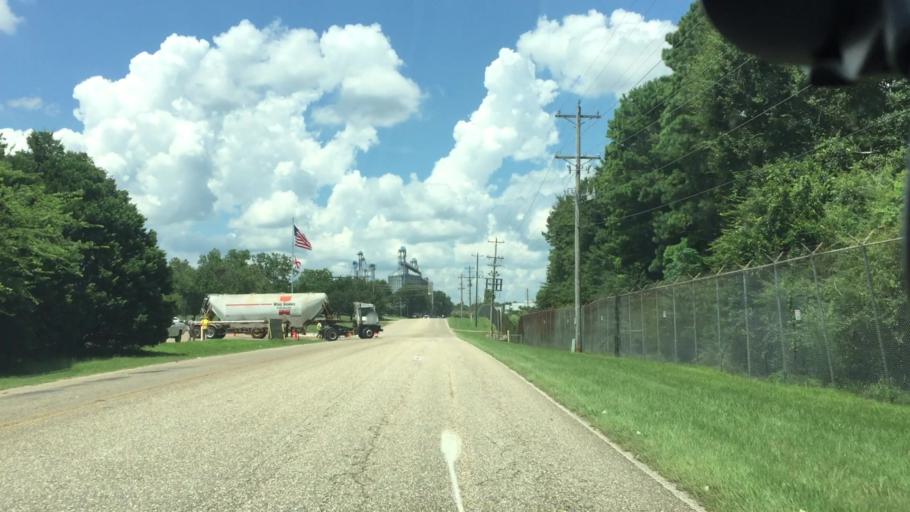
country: US
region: Alabama
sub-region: Pike County
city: Troy
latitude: 31.7796
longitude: -85.9793
